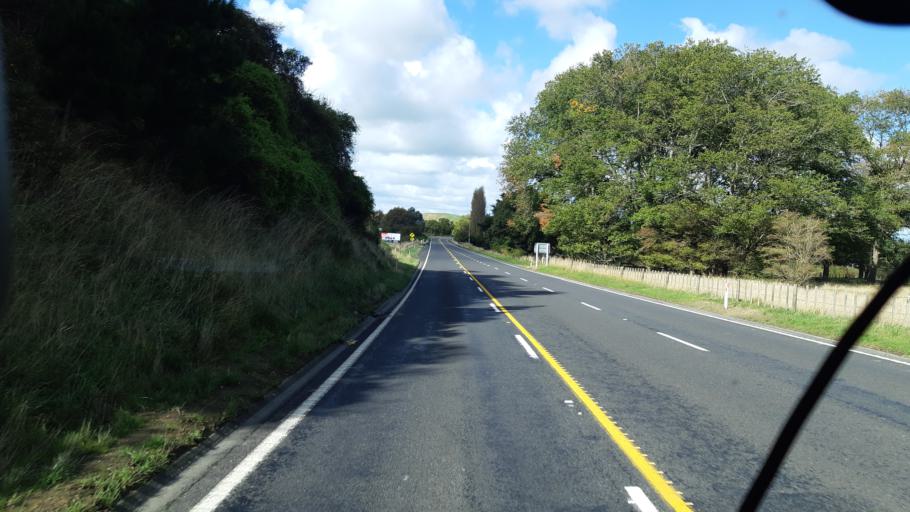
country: NZ
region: Manawatu-Wanganui
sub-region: Wanganui District
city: Wanganui
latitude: -40.0322
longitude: 175.2058
